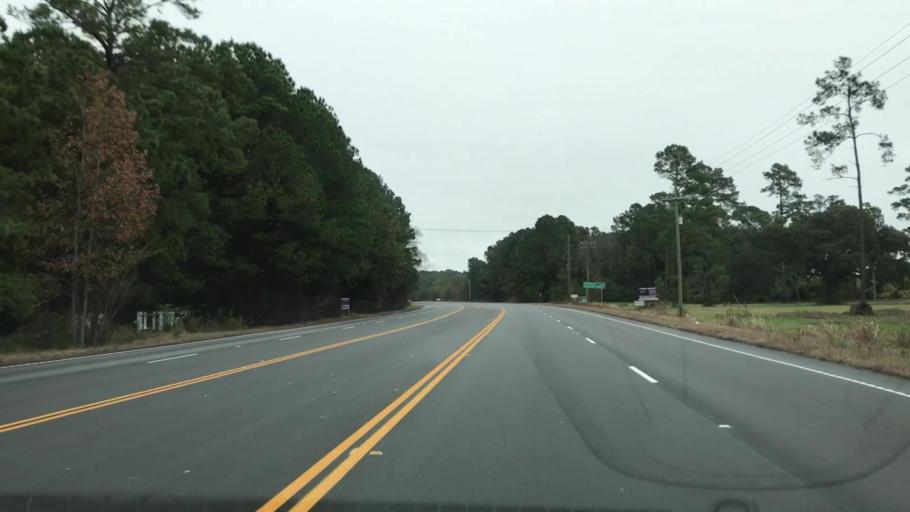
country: US
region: South Carolina
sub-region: Charleston County
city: Awendaw
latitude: 33.0989
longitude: -79.4706
